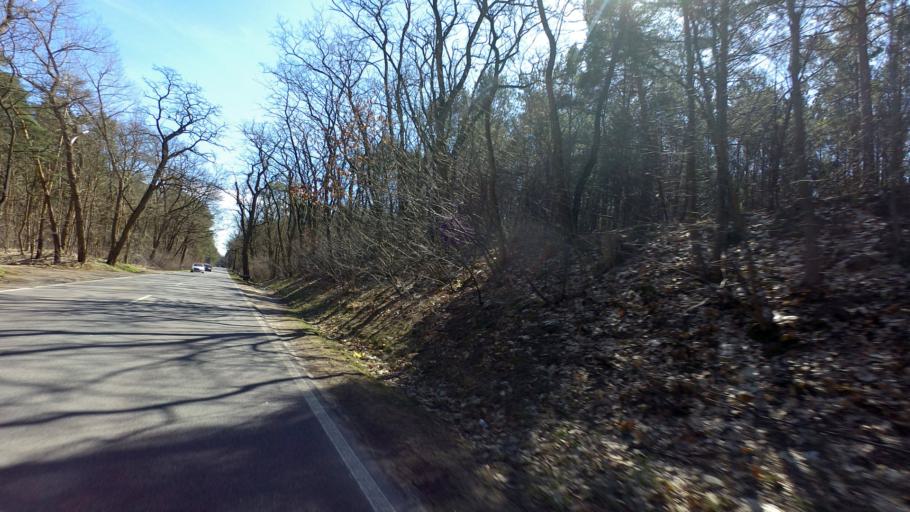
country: DE
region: Brandenburg
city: Teupitz
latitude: 52.1186
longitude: 13.6504
